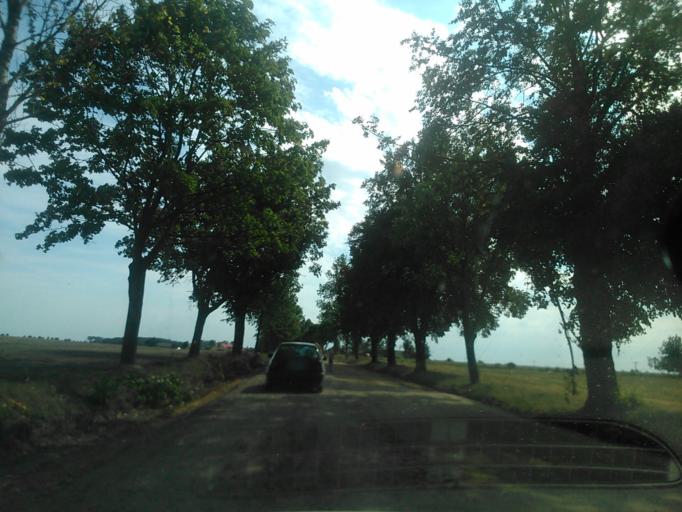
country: PL
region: Warmian-Masurian Voivodeship
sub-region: Powiat dzialdowski
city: Ilowo -Osada
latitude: 53.2036
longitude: 20.2411
